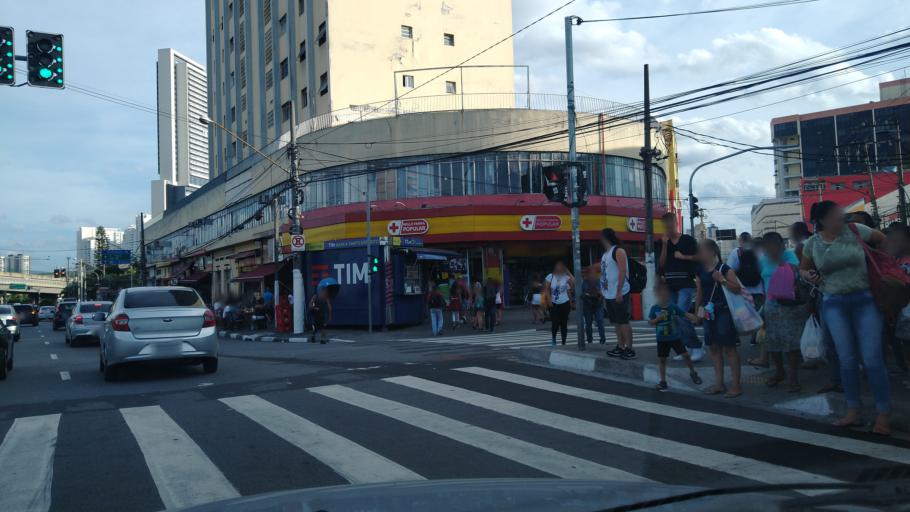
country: BR
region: Sao Paulo
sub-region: Osasco
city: Osasco
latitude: -23.5290
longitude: -46.7754
